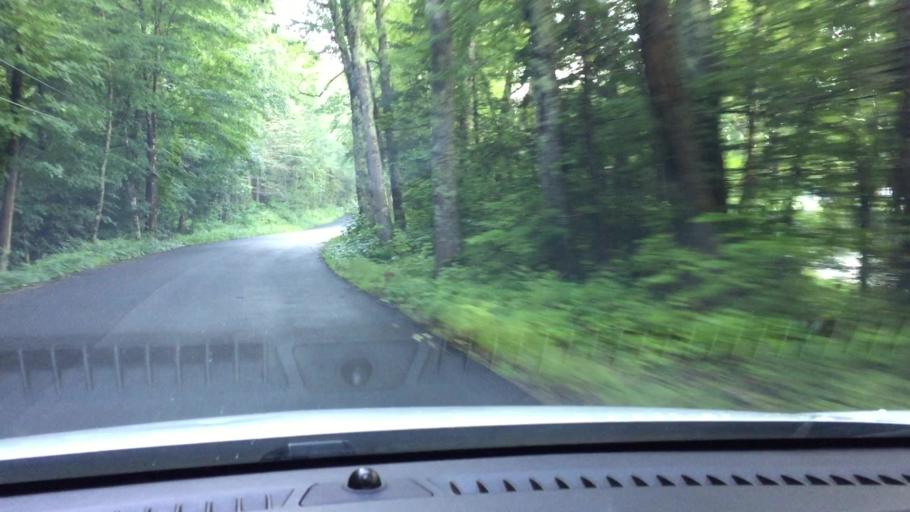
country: US
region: Massachusetts
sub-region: Hampshire County
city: Chesterfield
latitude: 42.3401
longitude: -72.9493
